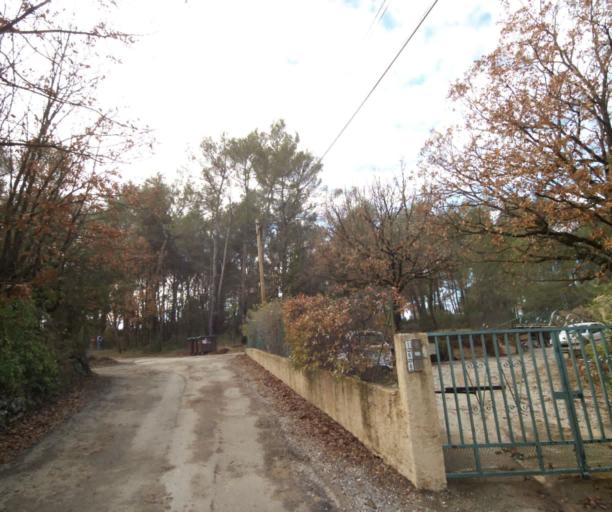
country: FR
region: Provence-Alpes-Cote d'Azur
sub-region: Departement du Var
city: Trans-en-Provence
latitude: 43.5179
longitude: 6.5000
